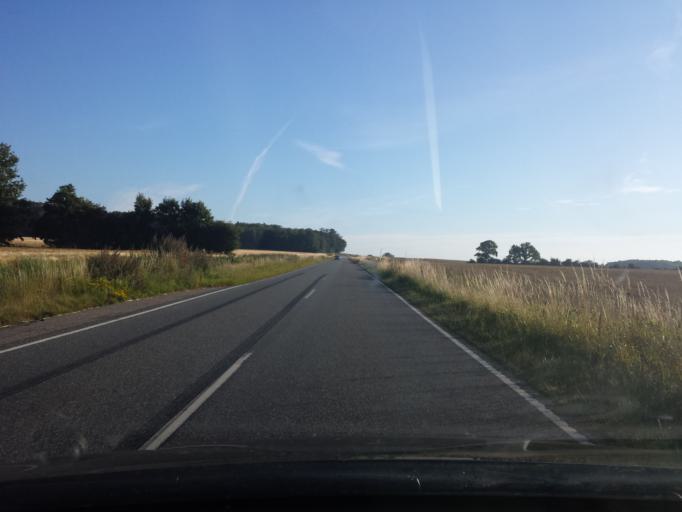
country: DK
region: South Denmark
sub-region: Sonderborg Kommune
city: Grasten
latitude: 54.9446
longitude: 9.6317
